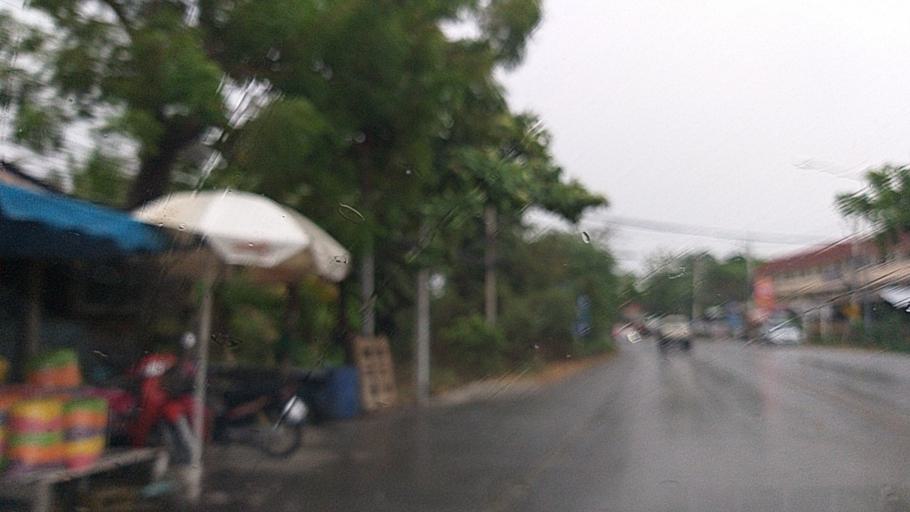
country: TH
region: Phra Nakhon Si Ayutthaya
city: Phra Nakhon Si Ayutthaya
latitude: 14.3432
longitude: 100.5809
